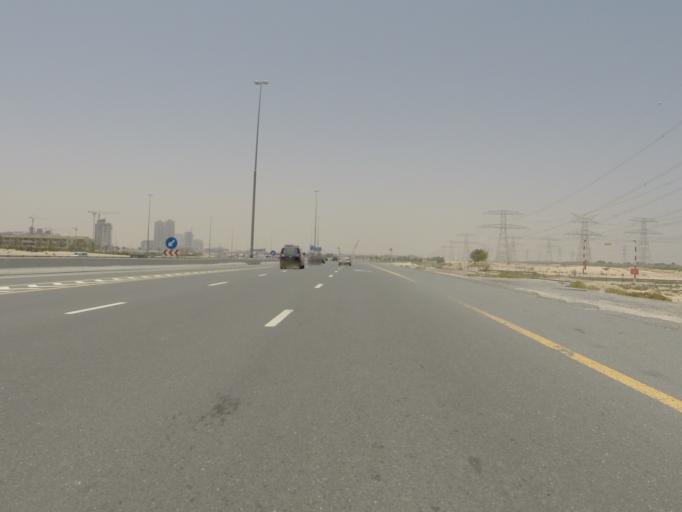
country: AE
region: Dubai
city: Dubai
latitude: 25.0633
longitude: 55.1979
